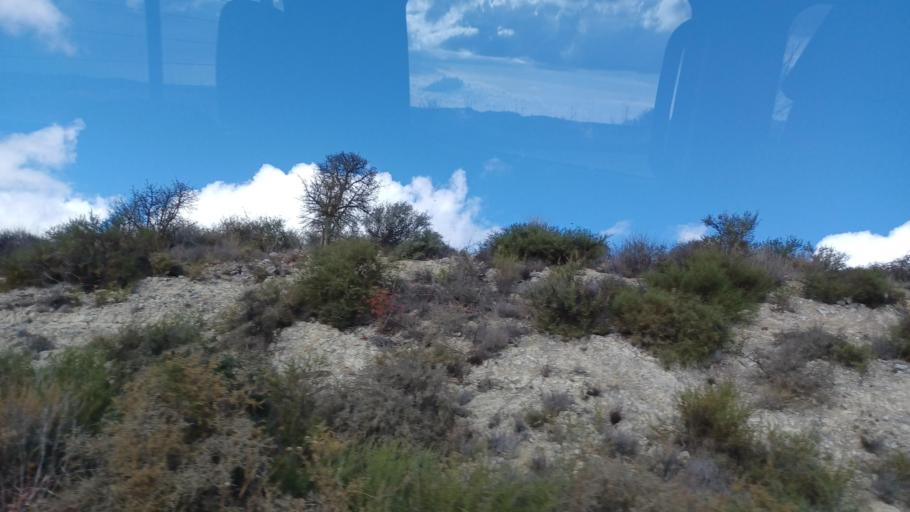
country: CY
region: Limassol
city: Pachna
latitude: 34.8345
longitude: 32.8079
